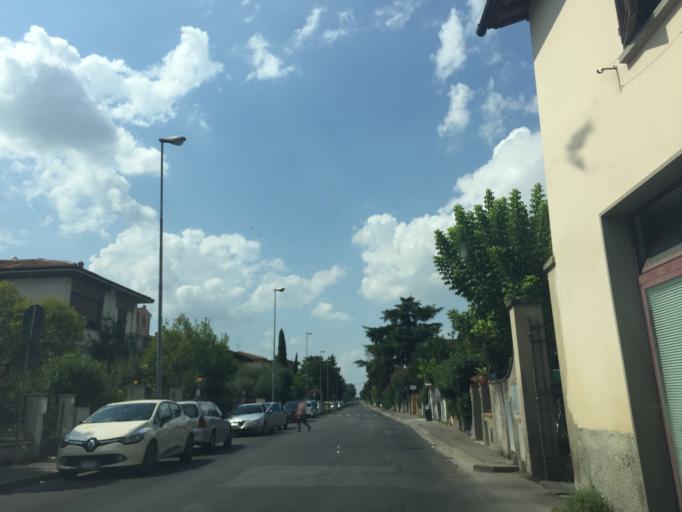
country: IT
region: Tuscany
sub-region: Province of Florence
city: San Donnino
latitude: 43.7970
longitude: 11.1471
